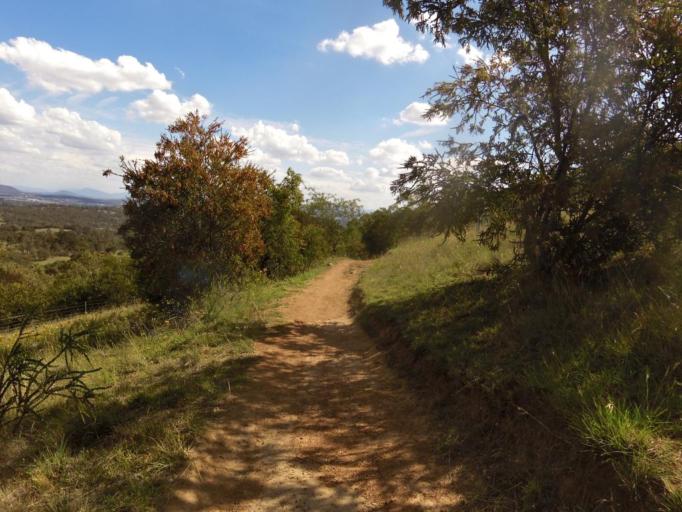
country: AU
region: Australian Capital Territory
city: Belconnen
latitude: -35.1501
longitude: 149.0887
